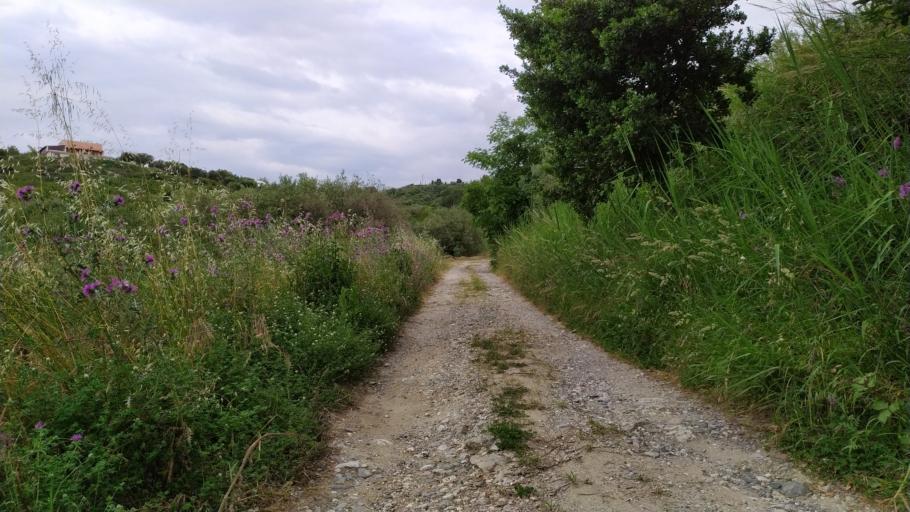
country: IT
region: Sicily
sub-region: Messina
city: Gualtieri Sicamino
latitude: 38.1565
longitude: 15.2988
